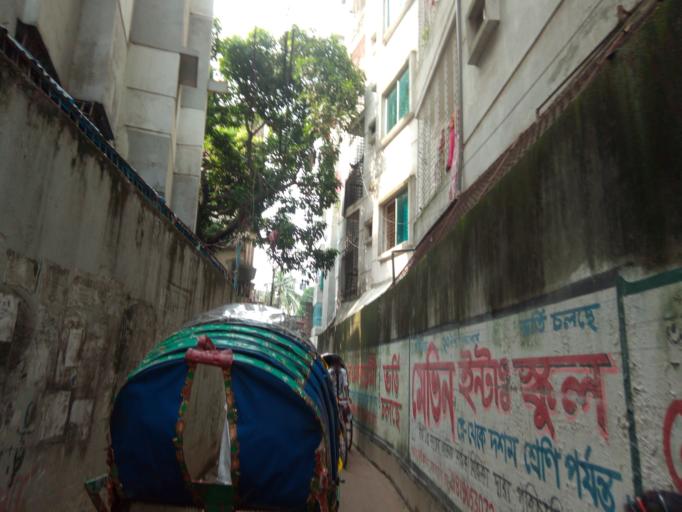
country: BD
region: Dhaka
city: Azimpur
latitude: 23.7412
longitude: 90.3656
